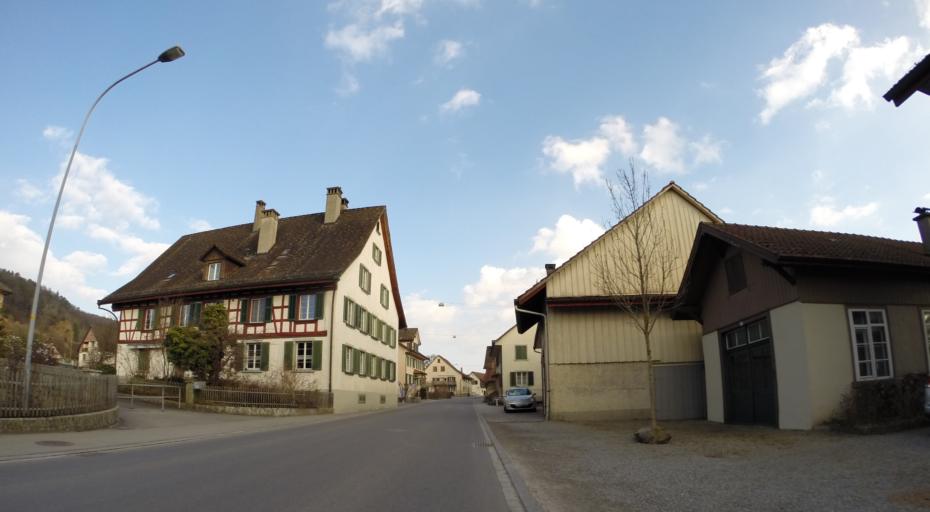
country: CH
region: Thurgau
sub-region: Frauenfeld District
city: Wagenhausen
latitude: 47.6336
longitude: 8.7964
